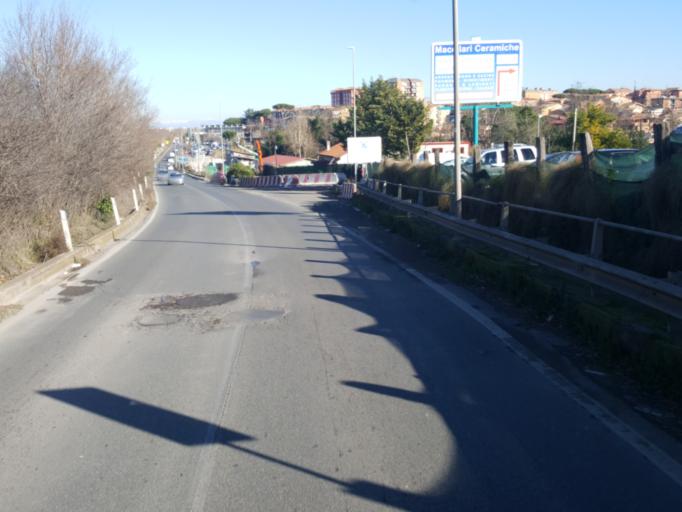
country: IT
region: Latium
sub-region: Citta metropolitana di Roma Capitale
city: Vitinia
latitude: 41.7876
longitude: 12.3722
